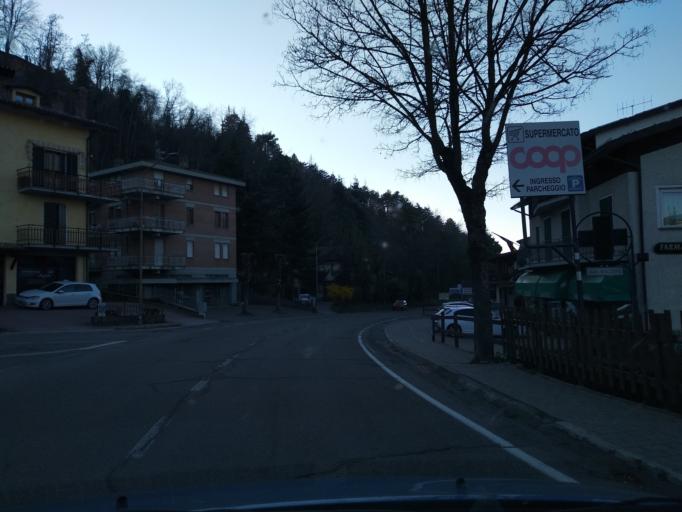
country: IT
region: Emilia-Romagna
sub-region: Provincia di Reggio Emilia
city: Castelnovo ne'Monti
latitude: 44.4371
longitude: 10.3997
